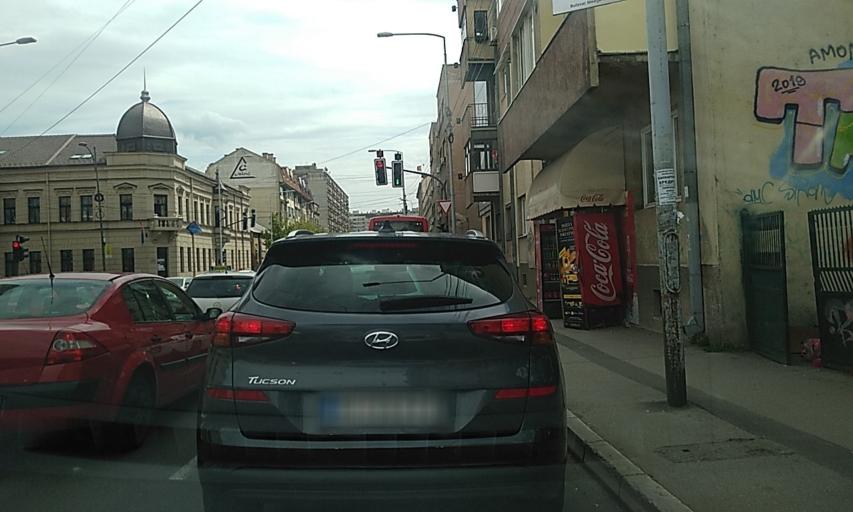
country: RS
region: Central Serbia
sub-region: Nisavski Okrug
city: Nis
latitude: 43.3206
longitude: 21.8908
